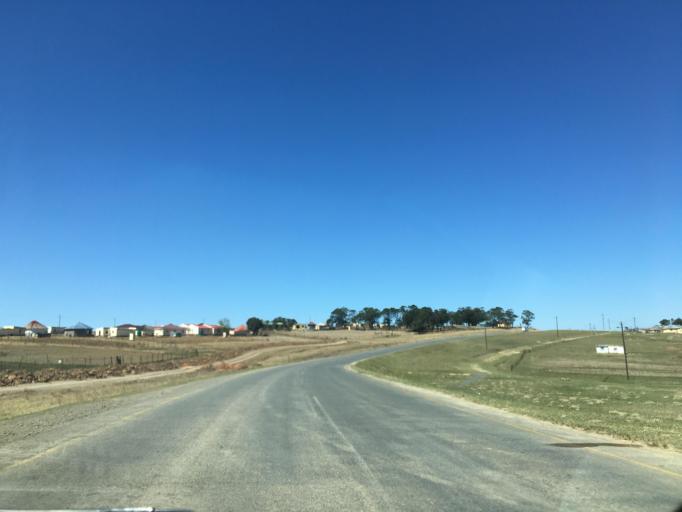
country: ZA
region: Eastern Cape
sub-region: Chris Hani District Municipality
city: Cala
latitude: -31.5513
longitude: 27.8928
